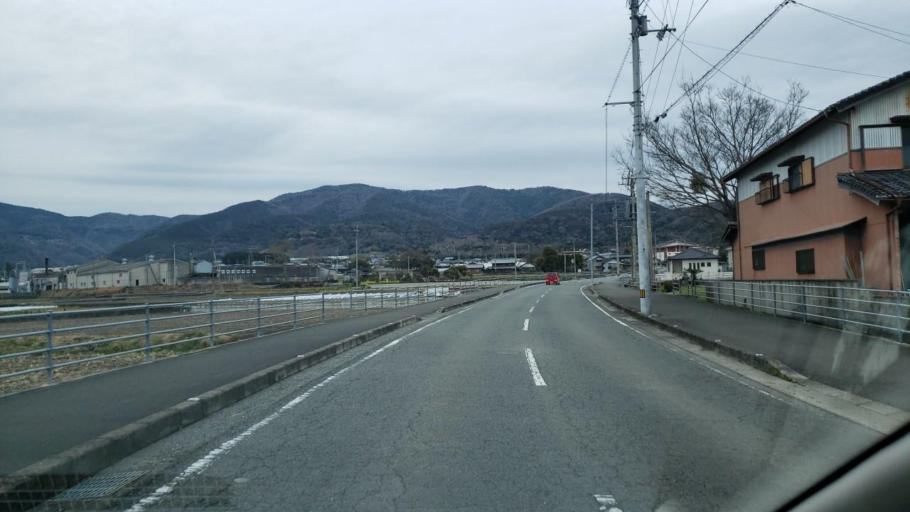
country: JP
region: Tokushima
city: Kamojimacho-jogejima
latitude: 34.1092
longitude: 134.3398
